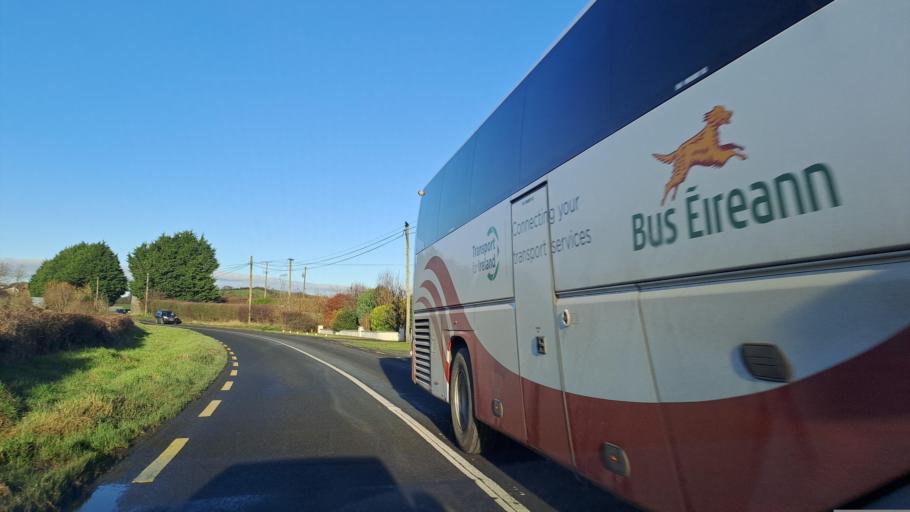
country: IE
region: Ulster
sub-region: An Cabhan
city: Bailieborough
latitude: 53.8878
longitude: -6.9626
